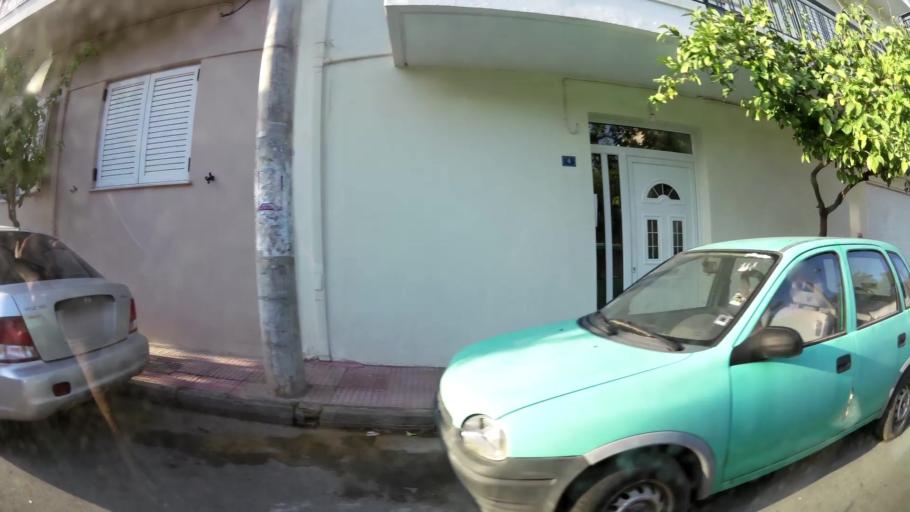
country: GR
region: Attica
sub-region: Nomarchia Athinas
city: Nea Filadelfeia
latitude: 38.0437
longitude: 23.7305
